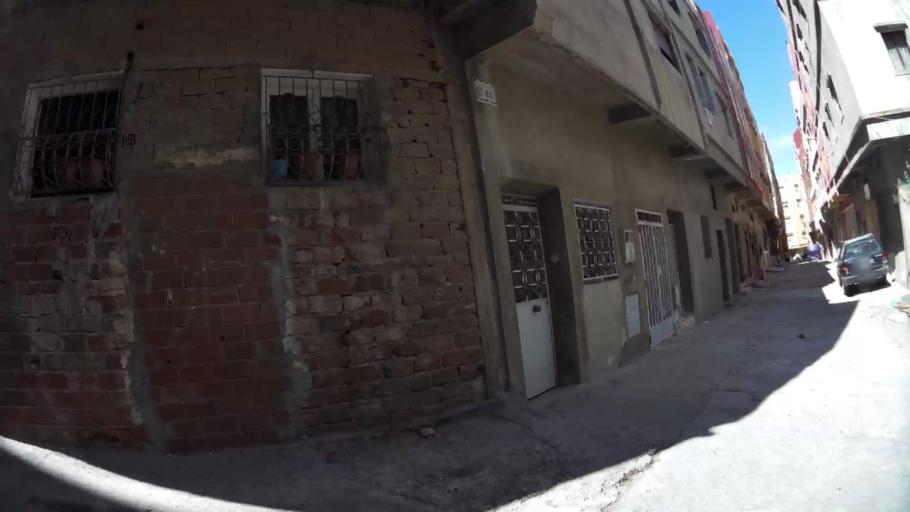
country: MA
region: Tanger-Tetouan
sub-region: Tanger-Assilah
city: Tangier
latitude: 35.7564
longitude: -5.8045
